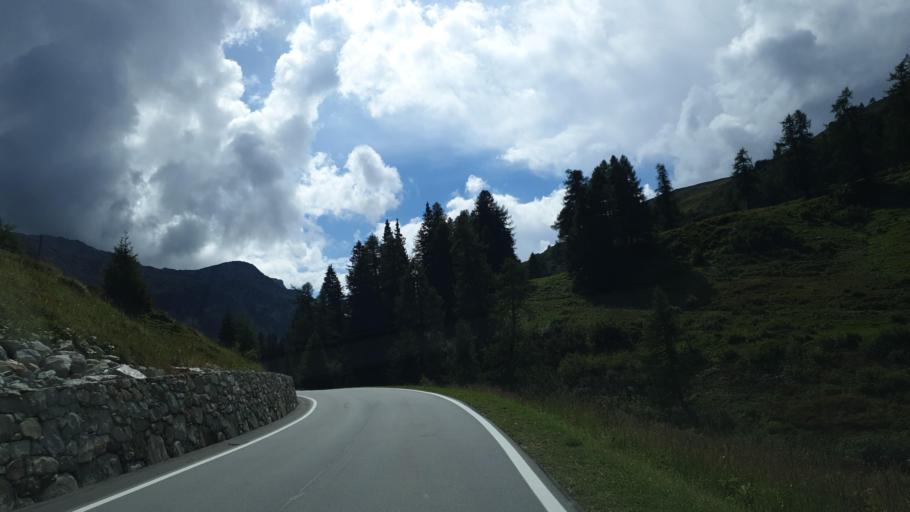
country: CH
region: Grisons
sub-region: Hinterrhein District
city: Hinterrhein
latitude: 46.5304
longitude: 9.3275
